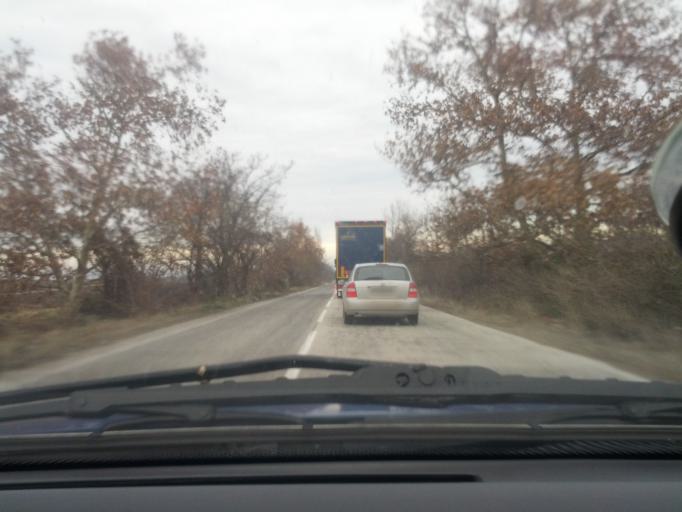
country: BG
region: Vratsa
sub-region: Obshtina Borovan
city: Borovan
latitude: 43.3255
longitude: 23.6867
